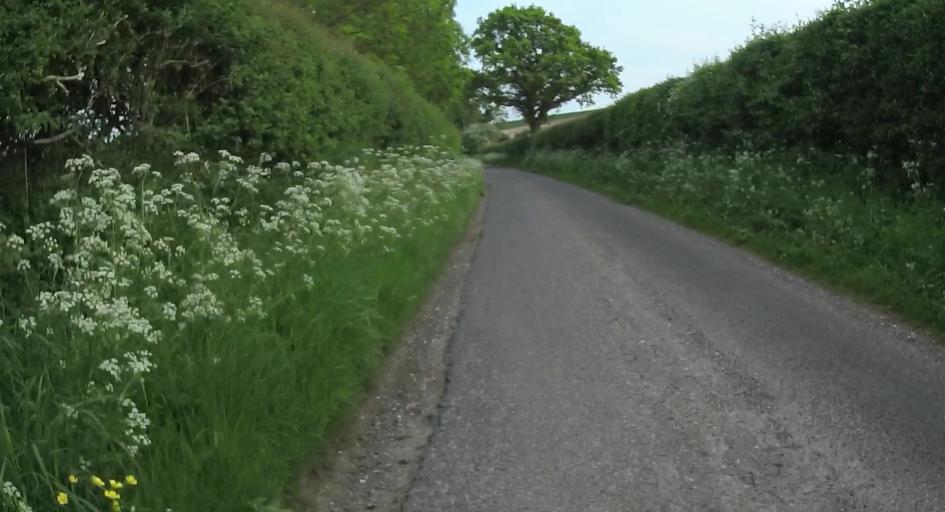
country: GB
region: England
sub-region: Hampshire
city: Overton
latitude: 51.2784
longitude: -1.2587
